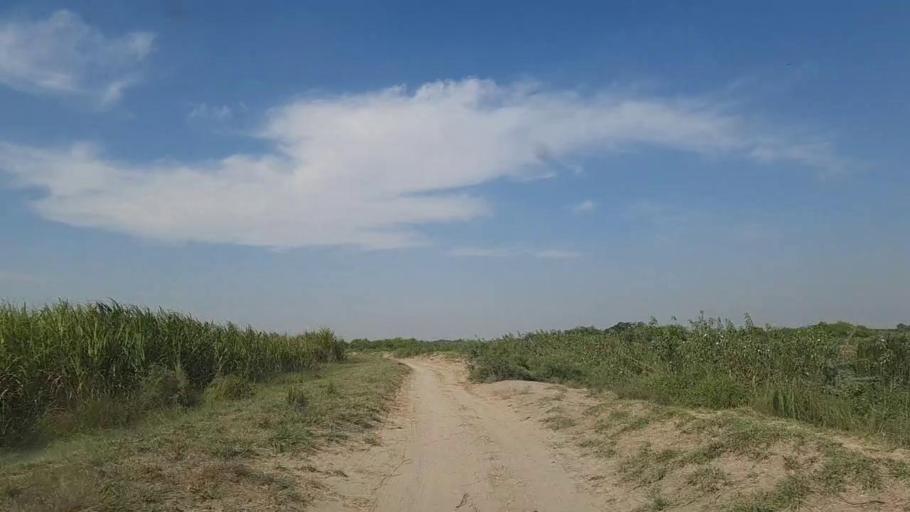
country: PK
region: Sindh
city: Mirpur Batoro
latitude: 24.8050
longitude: 68.2667
